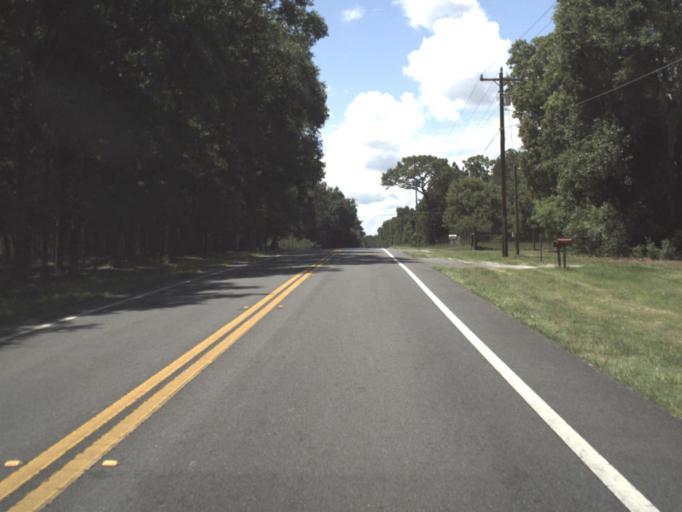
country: US
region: Florida
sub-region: Alachua County
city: Hawthorne
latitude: 29.6523
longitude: -82.0332
